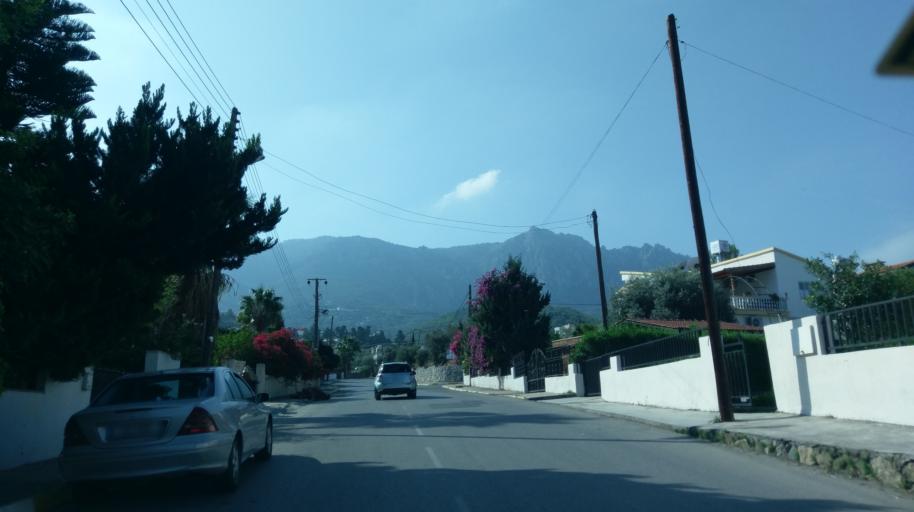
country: CY
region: Keryneia
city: Kyrenia
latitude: 35.3341
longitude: 33.2621
